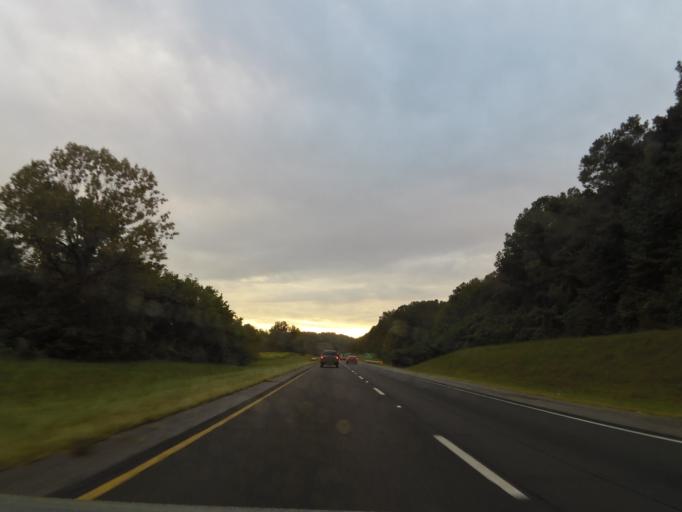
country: US
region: Alabama
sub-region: Jefferson County
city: Argo
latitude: 33.6682
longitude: -86.5558
